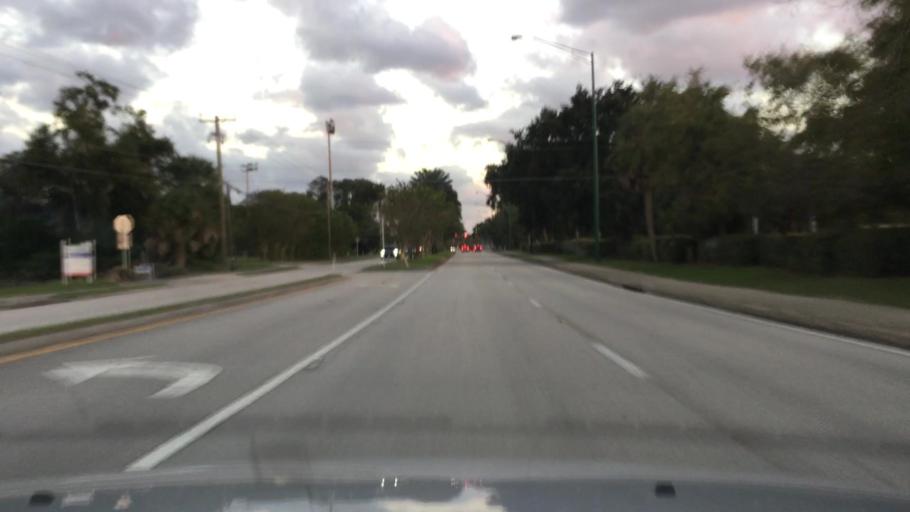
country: US
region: Florida
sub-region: Volusia County
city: Ormond Beach
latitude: 29.2885
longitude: -81.0851
